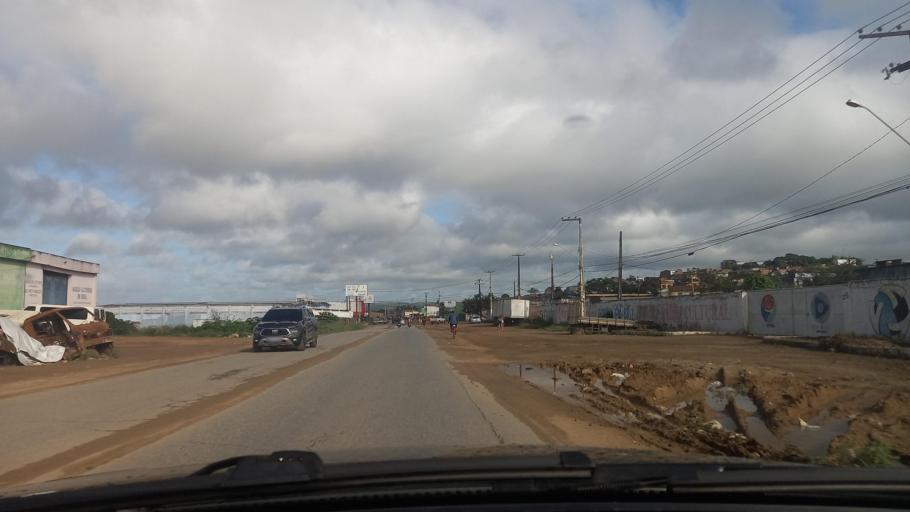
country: BR
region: Pernambuco
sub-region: Vitoria De Santo Antao
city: Vitoria de Santo Antao
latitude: -8.1172
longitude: -35.3094
